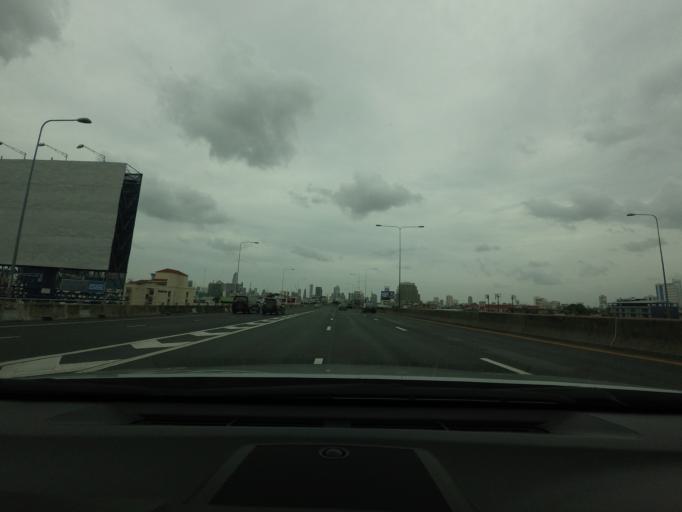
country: TH
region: Bangkok
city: Pom Prap Sattru Phai
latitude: 13.7542
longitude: 100.5233
